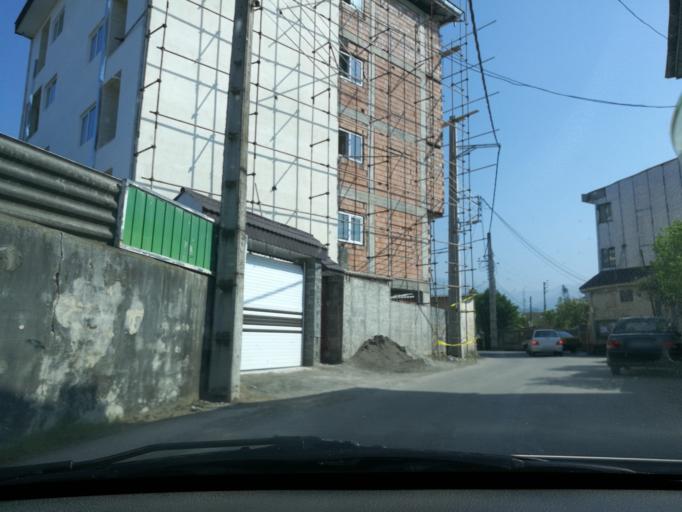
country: IR
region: Mazandaran
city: Chalus
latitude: 36.6664
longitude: 51.4315
